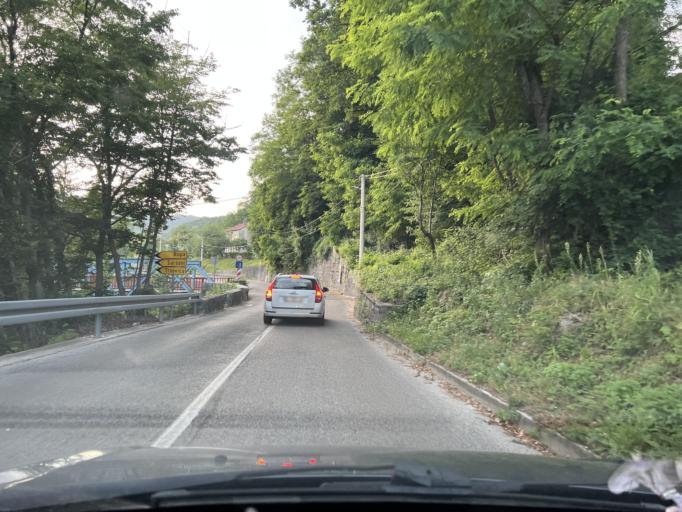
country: HR
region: Primorsko-Goranska
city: Marcelji
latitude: 45.3952
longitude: 14.4264
